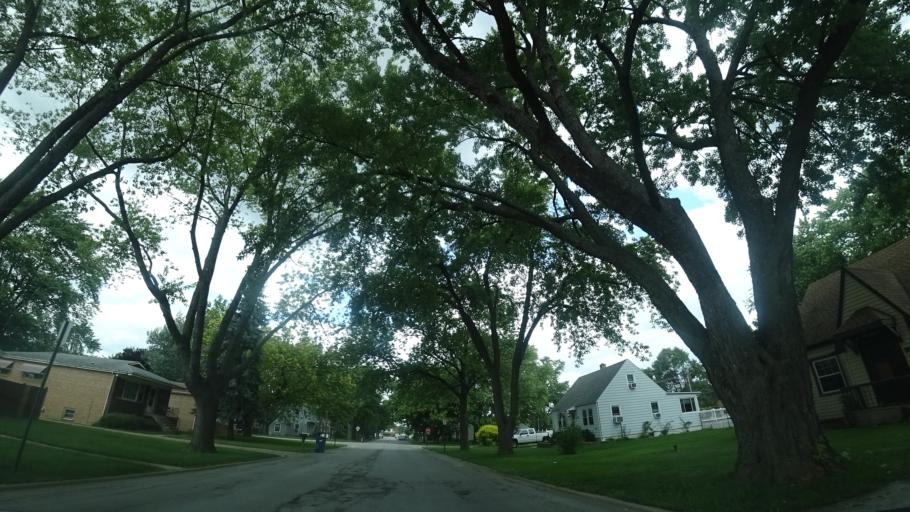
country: US
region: Illinois
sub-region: Cook County
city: Alsip
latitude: 41.6815
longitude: -87.7223
